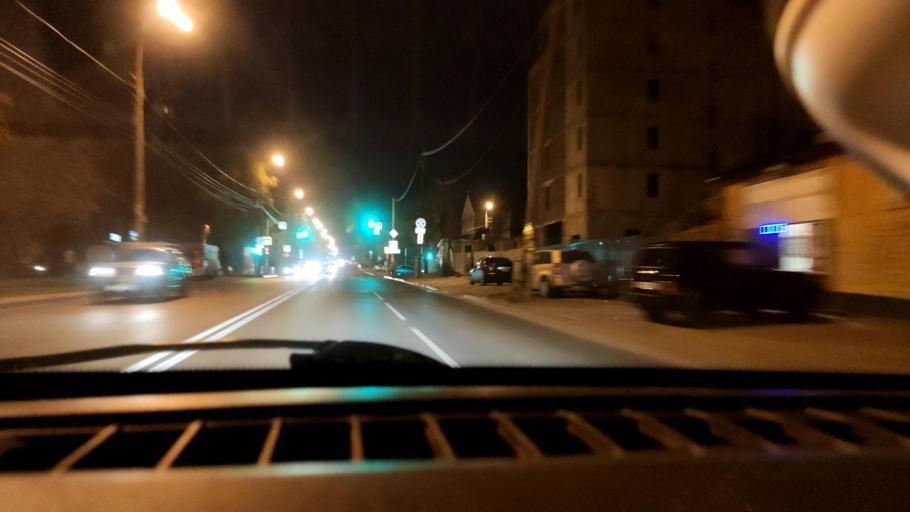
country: RU
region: Samara
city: Samara
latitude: 53.1975
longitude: 50.2053
